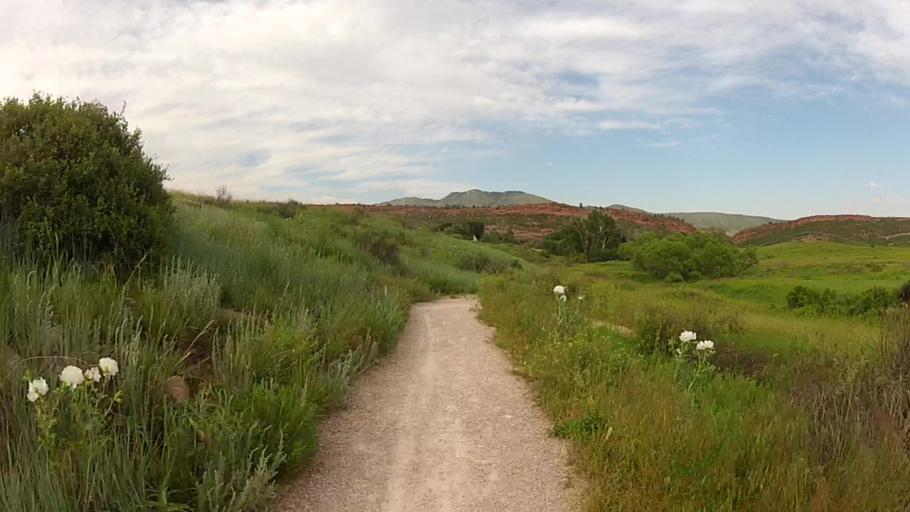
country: US
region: Colorado
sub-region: Larimer County
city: Laporte
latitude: 40.4816
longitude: -105.2310
